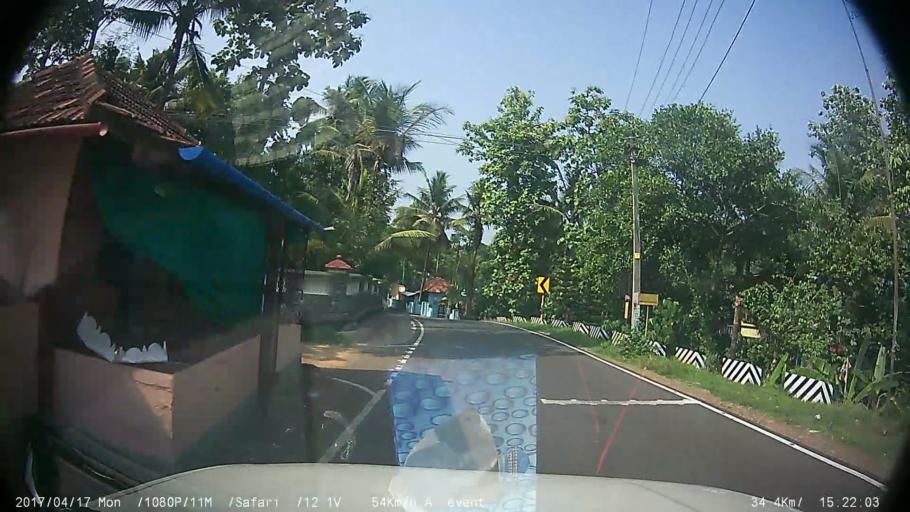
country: IN
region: Kerala
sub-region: Ernakulam
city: Ramamangalam
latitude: 9.9351
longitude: 76.4515
